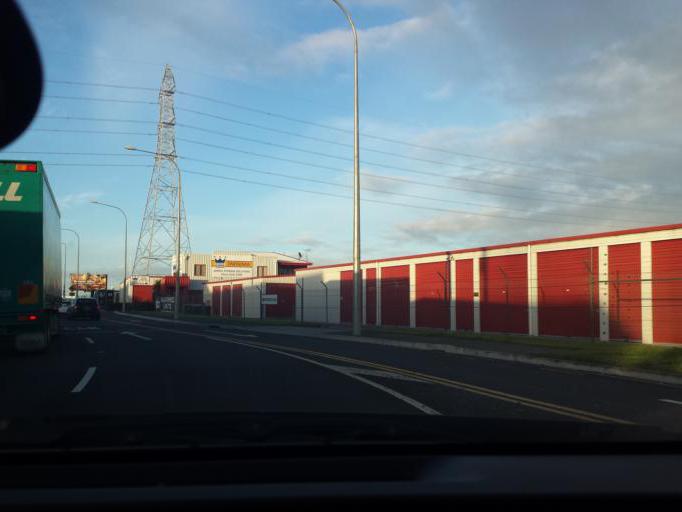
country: NZ
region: Auckland
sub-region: Auckland
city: Mangere
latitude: -36.9269
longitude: 174.7825
